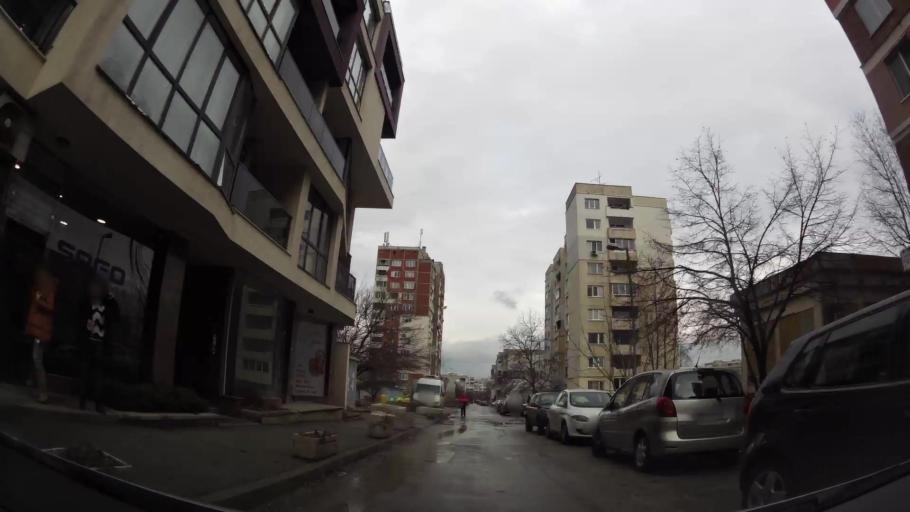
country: BG
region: Sofiya
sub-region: Obshtina Bozhurishte
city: Bozhurishte
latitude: 42.7232
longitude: 23.2523
